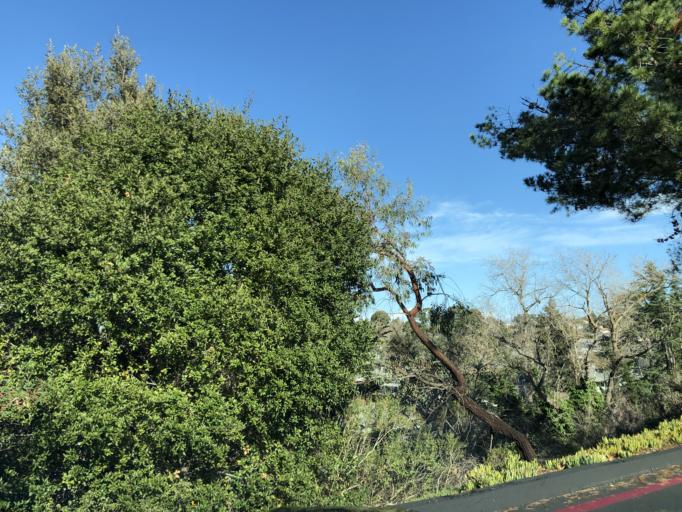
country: US
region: California
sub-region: Contra Costa County
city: Tara Hills
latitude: 37.9837
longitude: -122.3080
